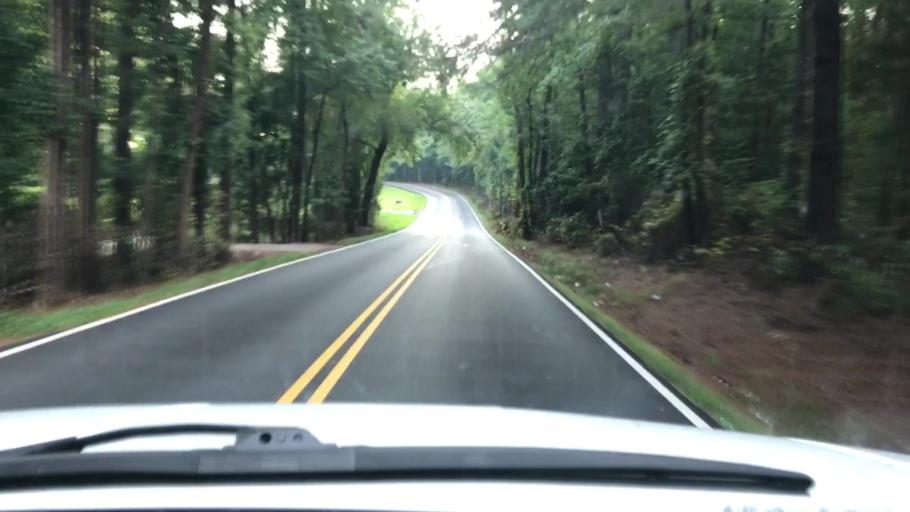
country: US
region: Virginia
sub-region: Chesterfield County
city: Chesterfield
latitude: 37.4165
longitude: -77.5453
